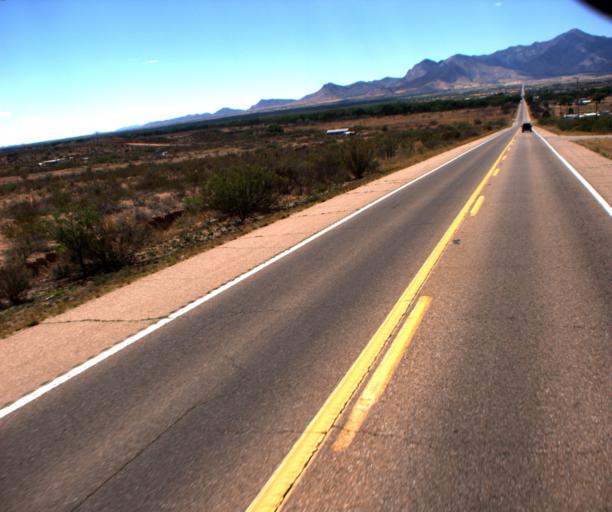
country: US
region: Arizona
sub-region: Cochise County
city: Sierra Vista Southeast
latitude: 31.3800
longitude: -110.0959
